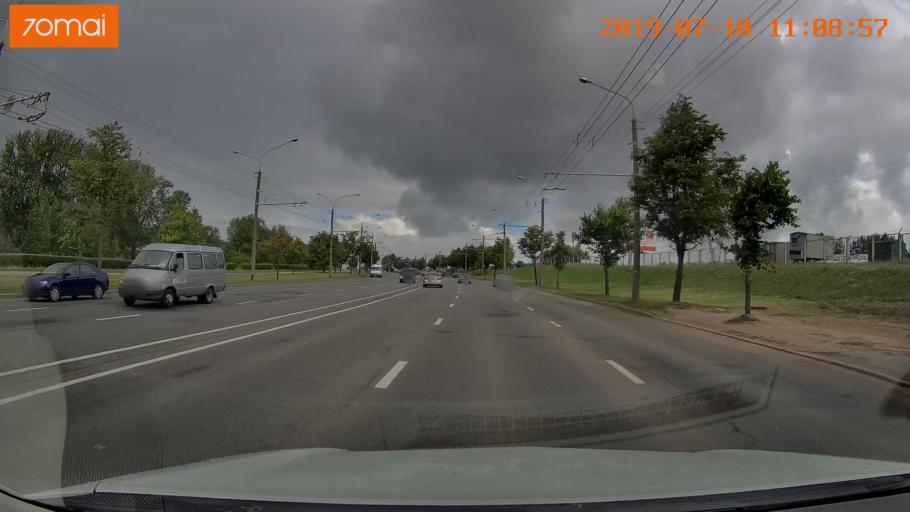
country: BY
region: Minsk
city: Syenitsa
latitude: 53.8597
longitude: 27.5379
